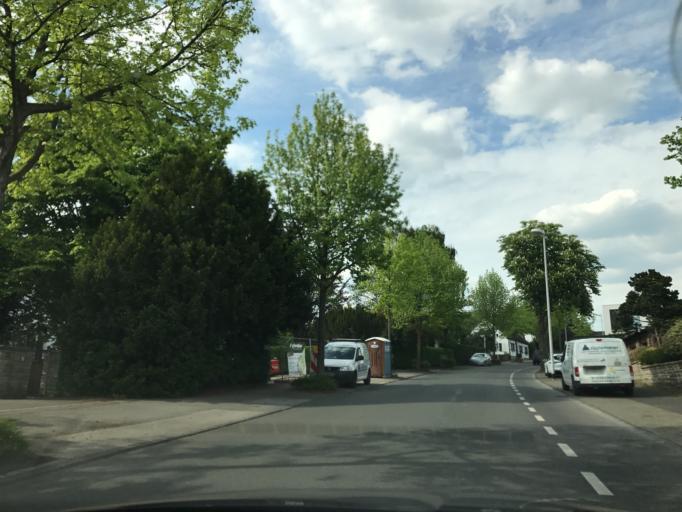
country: DE
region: North Rhine-Westphalia
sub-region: Regierungsbezirk Dusseldorf
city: Muelheim (Ruhr)
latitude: 51.4065
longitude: 6.9033
